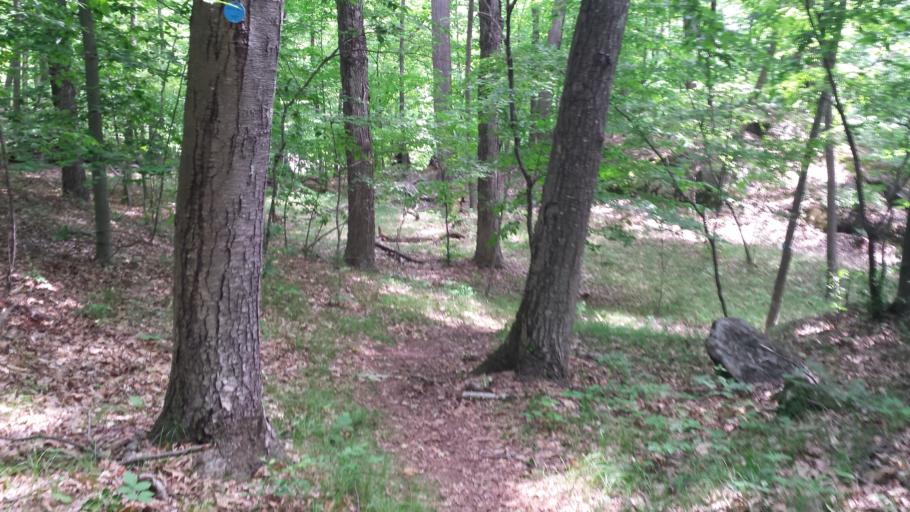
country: US
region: New York
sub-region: Westchester County
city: Yorktown Heights
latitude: 41.2645
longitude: -73.7358
